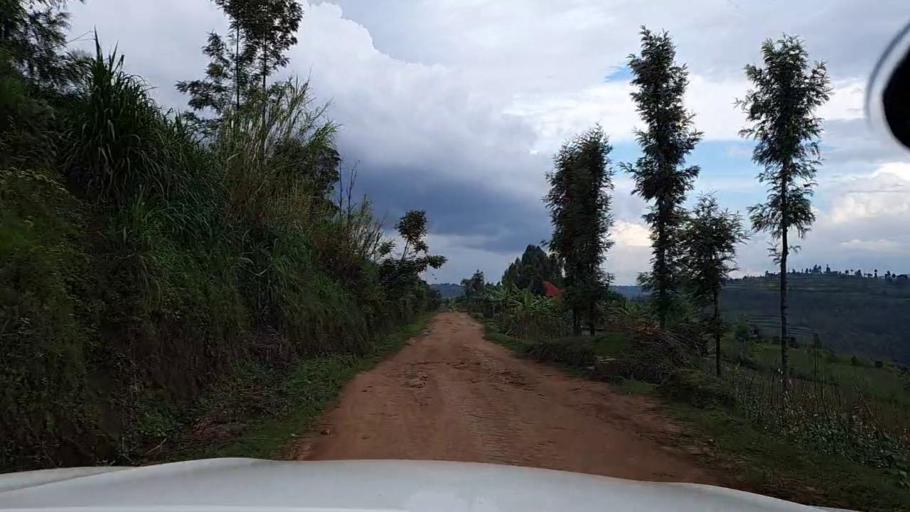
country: BI
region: Kayanza
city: Kayanza
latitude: -2.7955
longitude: 29.5154
